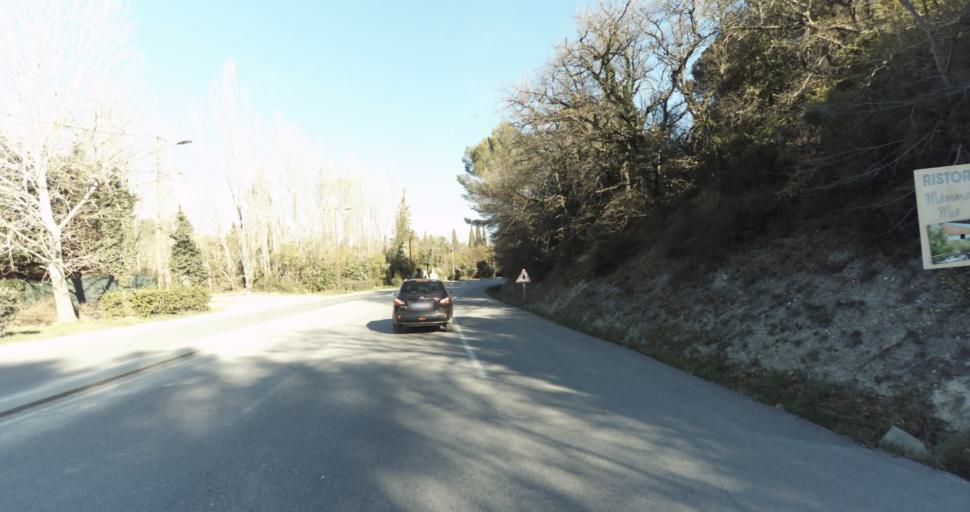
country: FR
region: Provence-Alpes-Cote d'Azur
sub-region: Departement des Bouches-du-Rhone
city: Aix-en-Provence
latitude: 43.5535
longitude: 5.4348
